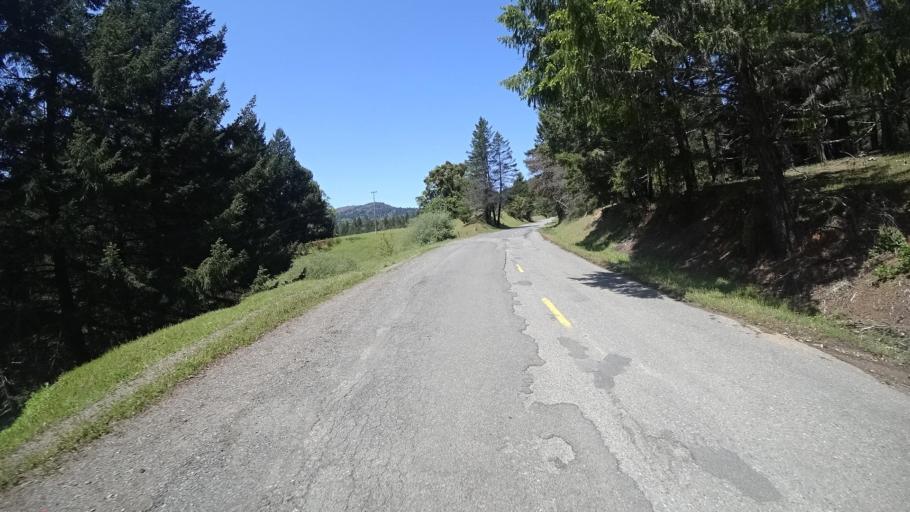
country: US
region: California
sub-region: Humboldt County
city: Redway
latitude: 40.1204
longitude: -123.6458
